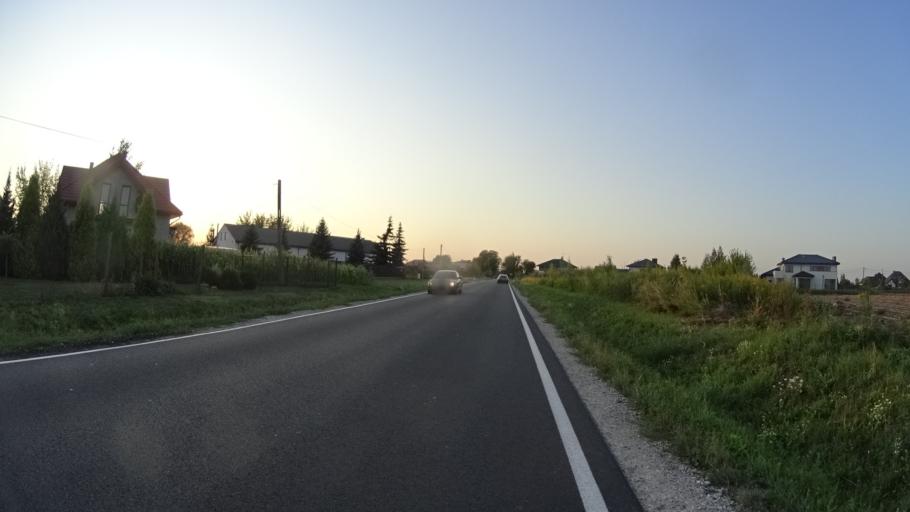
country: PL
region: Masovian Voivodeship
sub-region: Powiat warszawski zachodni
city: Ozarow Mazowiecki
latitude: 52.2446
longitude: 20.7473
